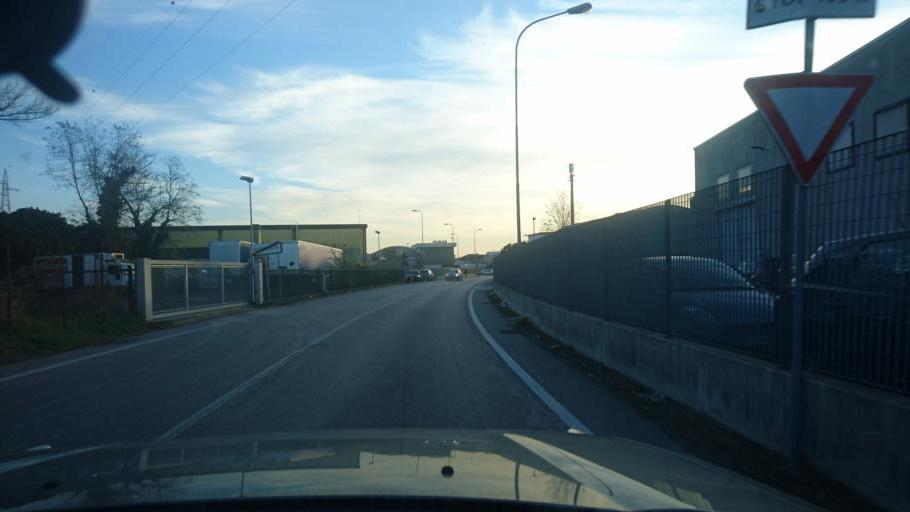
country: IT
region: Veneto
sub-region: Provincia di Padova
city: Noventa
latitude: 45.4156
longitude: 11.9369
